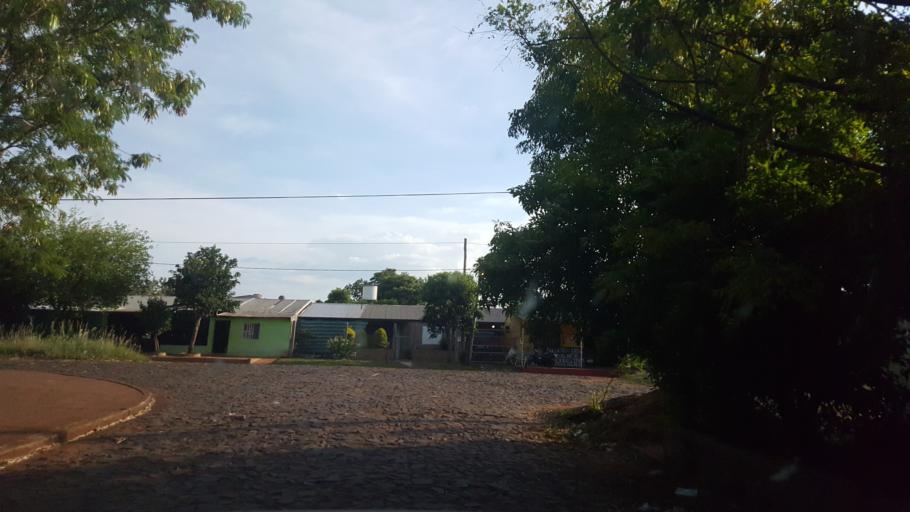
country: AR
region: Misiones
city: Garupa
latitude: -27.4354
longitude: -55.8754
